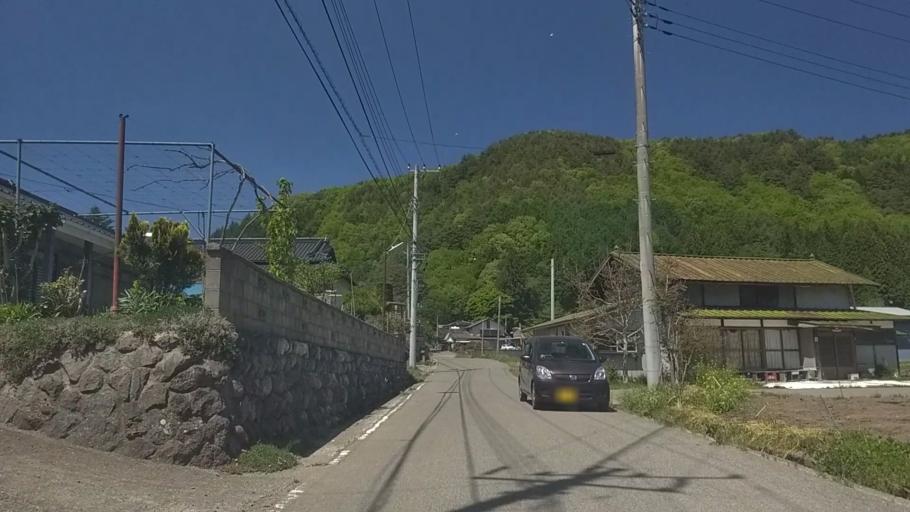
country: JP
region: Yamanashi
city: Nirasaki
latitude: 35.8748
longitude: 138.4532
